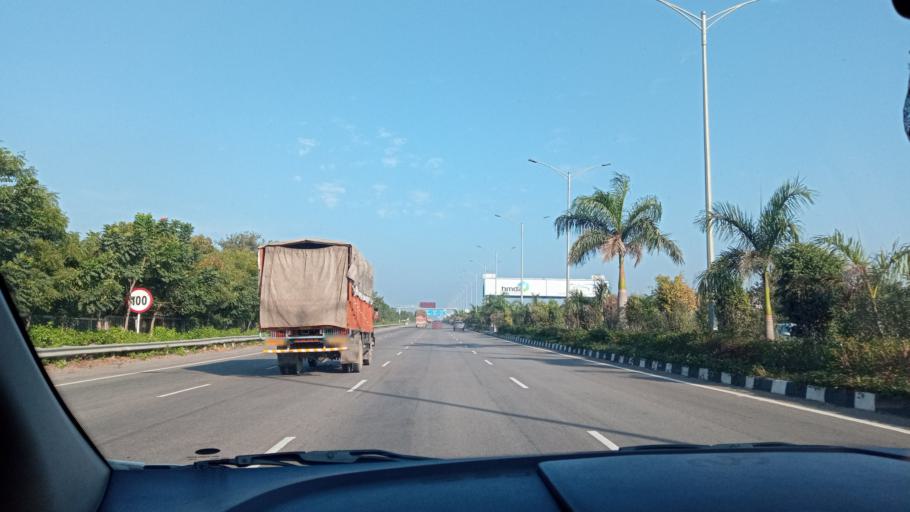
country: IN
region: Telangana
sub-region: Hyderabad
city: Hyderabad
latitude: 17.3324
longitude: 78.3702
